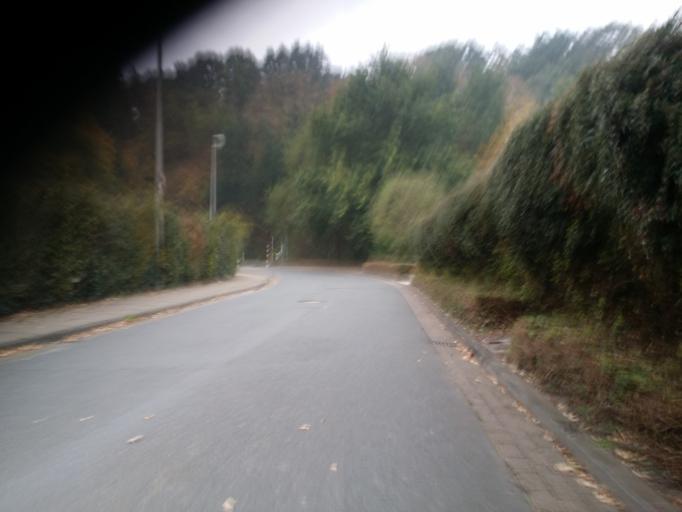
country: DE
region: Lower Saxony
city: Lemwerder
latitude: 53.1613
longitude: 8.6468
